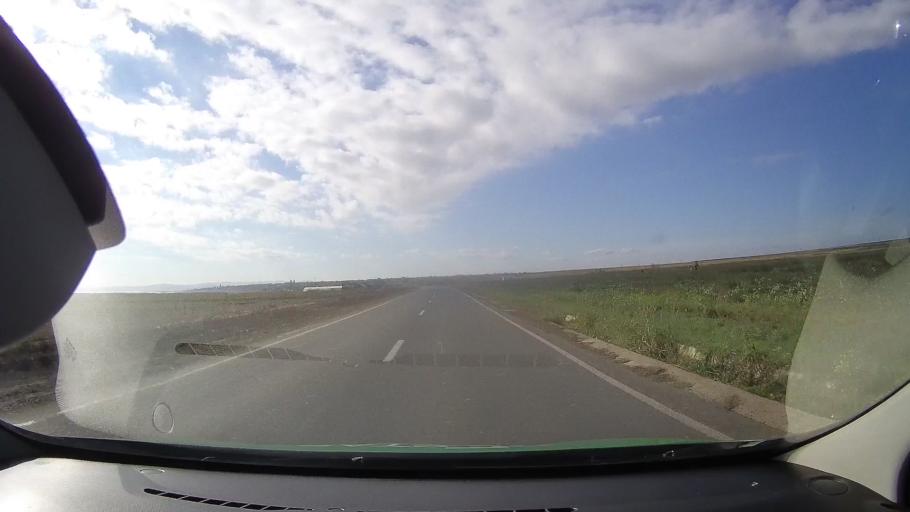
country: RO
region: Tulcea
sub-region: Comuna Sarichioi
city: Sarichioi
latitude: 44.9666
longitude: 28.8659
